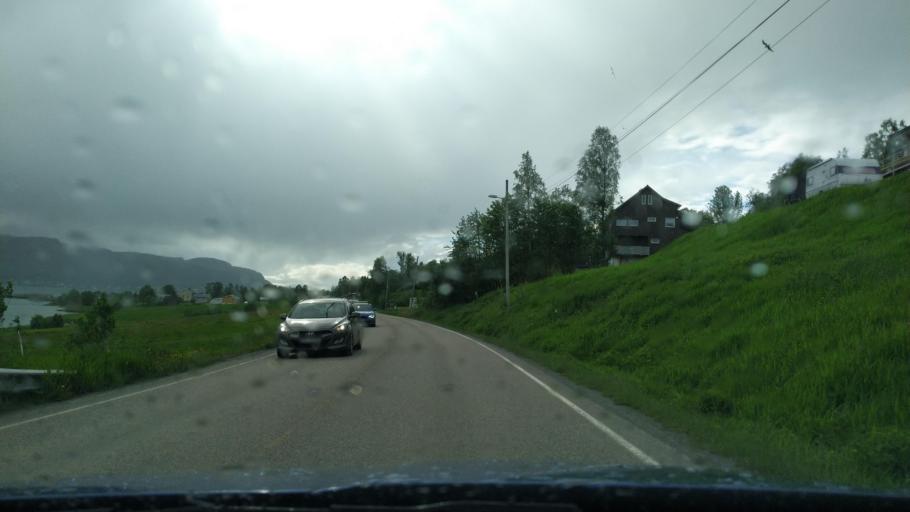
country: NO
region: Troms
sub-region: Sorreisa
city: Sorreisa
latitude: 69.1609
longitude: 18.1422
